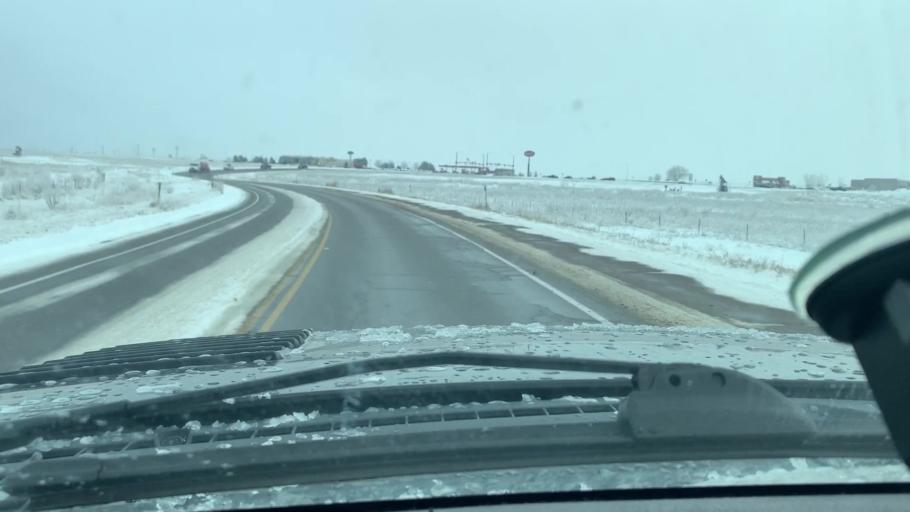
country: US
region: Colorado
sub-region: Weld County
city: Dacono
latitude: 40.0909
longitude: -104.9786
